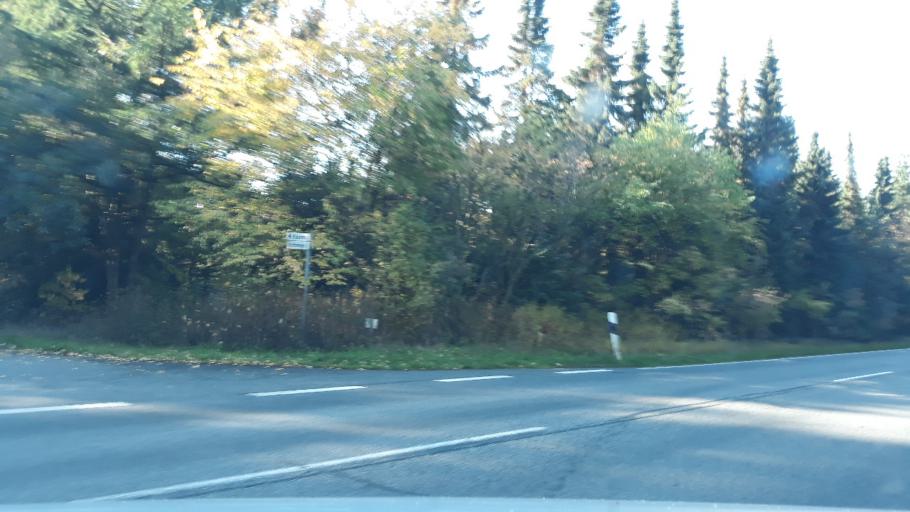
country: DE
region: Schleswig-Holstein
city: Kropp
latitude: 54.4030
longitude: 9.4988
